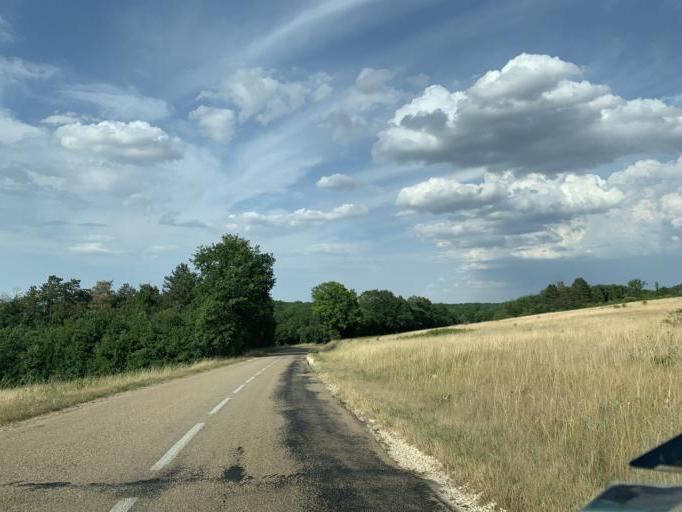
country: FR
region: Bourgogne
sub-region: Departement de l'Yonne
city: Fontenailles
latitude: 47.5299
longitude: 3.3893
